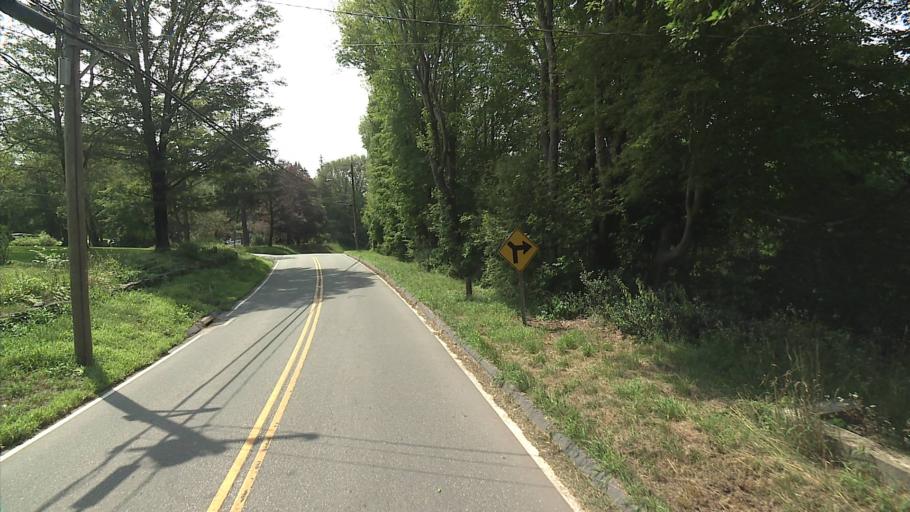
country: US
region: Connecticut
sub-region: Windham County
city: Moosup
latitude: 41.7236
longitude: -71.8693
